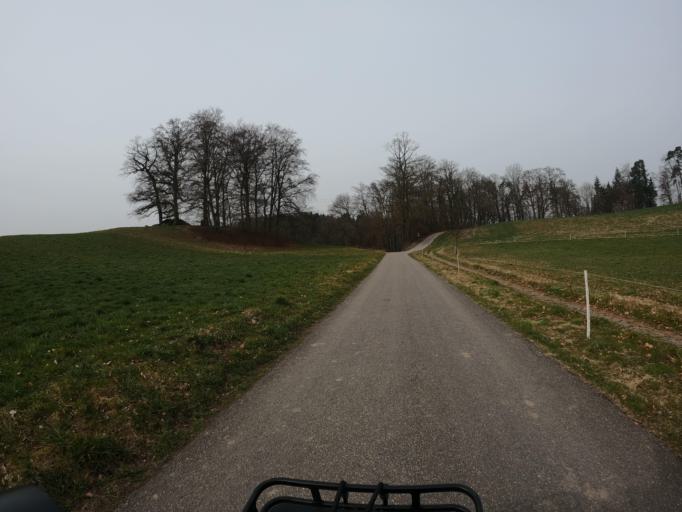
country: CH
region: Aargau
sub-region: Bezirk Baden
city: Mellingen
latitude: 47.4166
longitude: 8.2500
